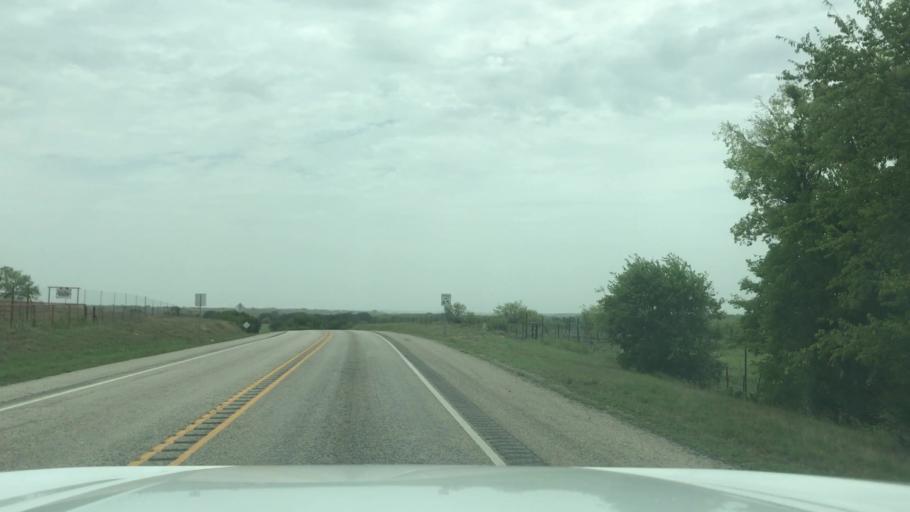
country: US
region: Texas
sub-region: Erath County
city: Dublin
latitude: 32.0580
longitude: -98.2011
